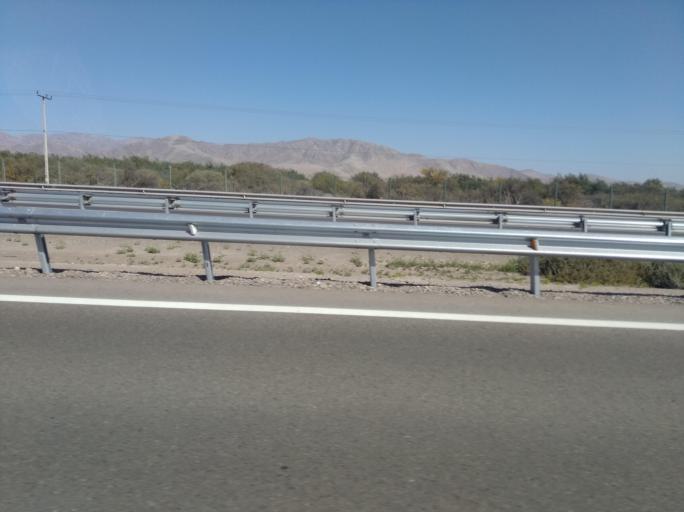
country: CL
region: Atacama
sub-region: Provincia de Copiapo
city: Copiapo
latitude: -27.3321
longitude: -70.5759
